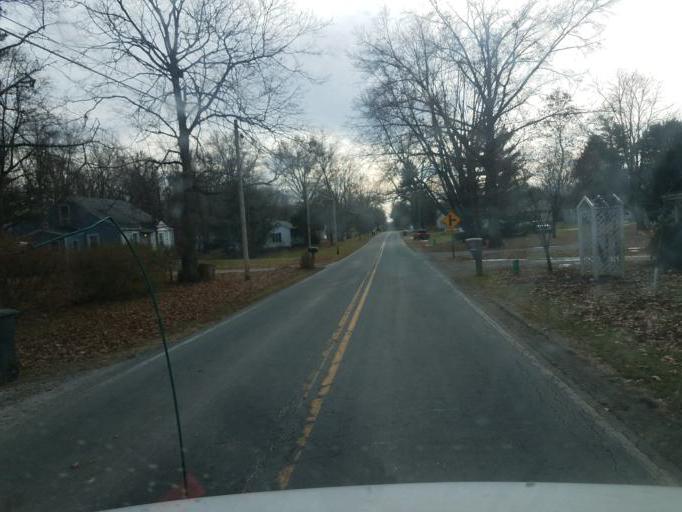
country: US
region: Ohio
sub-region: Delaware County
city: Ashley
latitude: 40.3280
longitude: -82.9577
